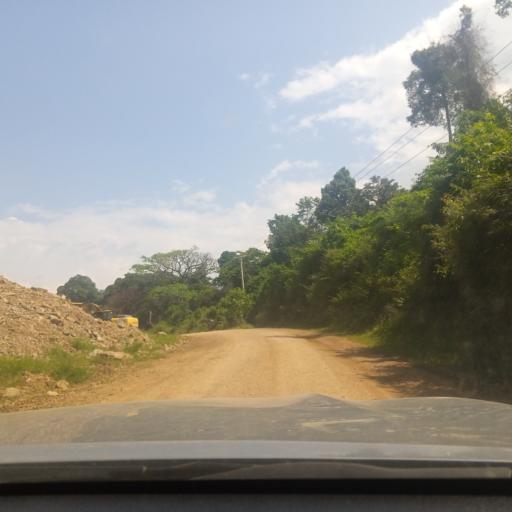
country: ET
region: Southern Nations, Nationalities, and People's Region
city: Tippi
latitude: 7.0707
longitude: 35.4354
